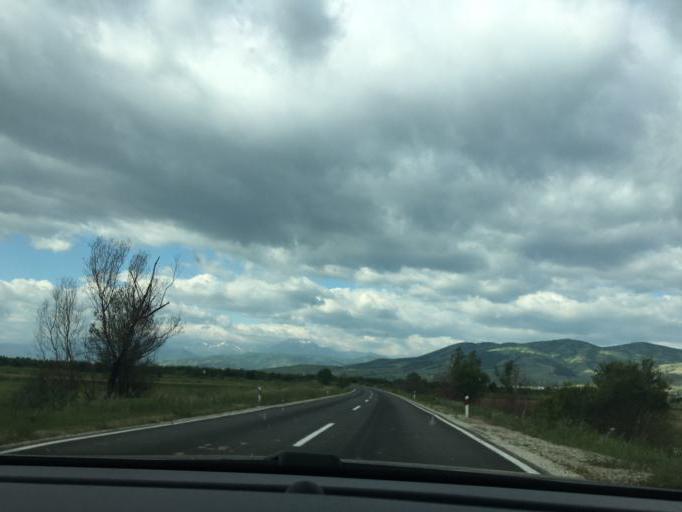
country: MK
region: Mogila
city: Dolno Srpci
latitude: 41.1768
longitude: 21.3936
